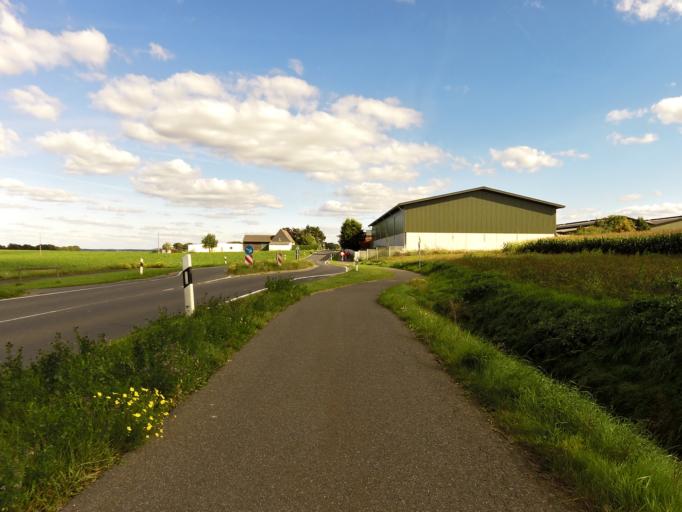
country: DE
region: North Rhine-Westphalia
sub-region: Regierungsbezirk Koln
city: Rheinbach
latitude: 50.6275
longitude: 6.9040
